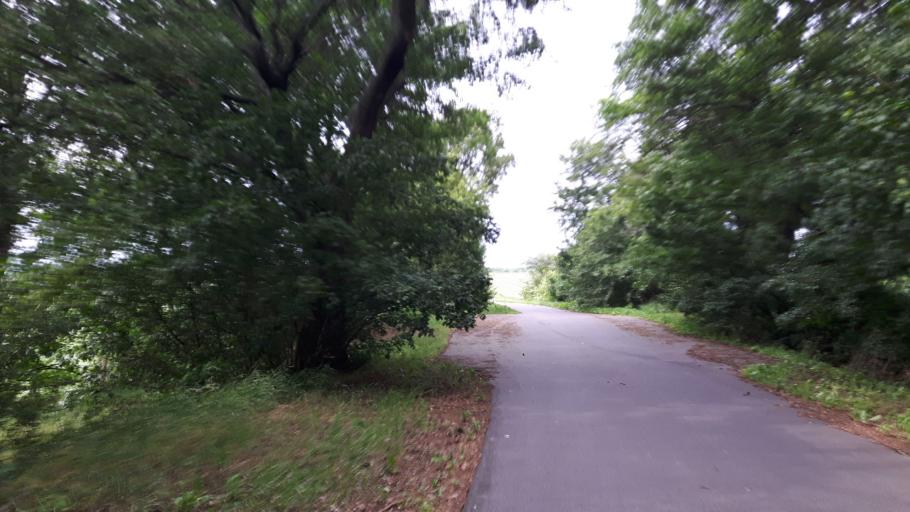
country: DE
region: Saxony
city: Rackwitz
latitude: 51.4164
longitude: 12.3195
